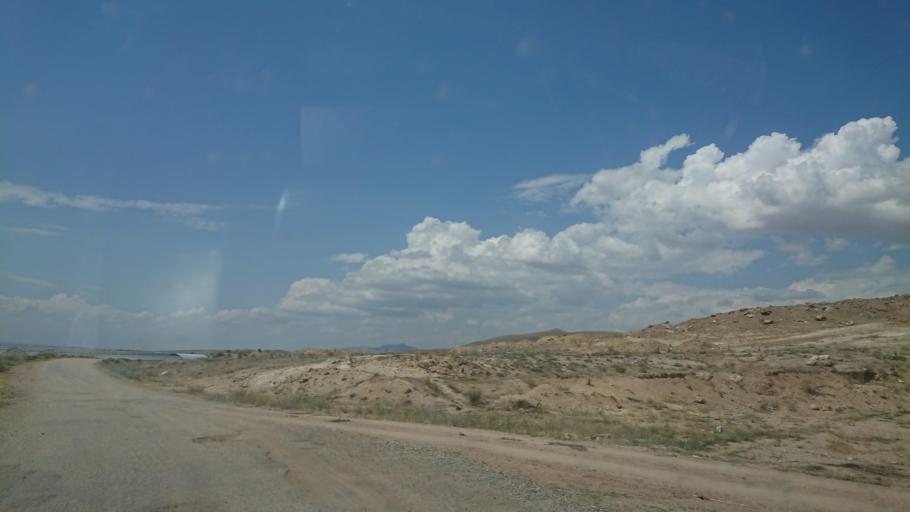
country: TR
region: Aksaray
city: Sariyahsi
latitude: 38.9966
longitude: 33.9151
